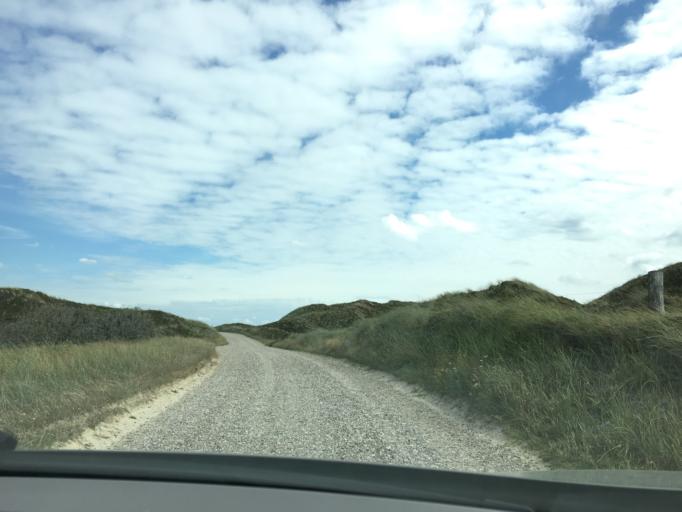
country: DK
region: South Denmark
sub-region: Varde Kommune
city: Oksbol
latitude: 55.7204
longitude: 8.1739
